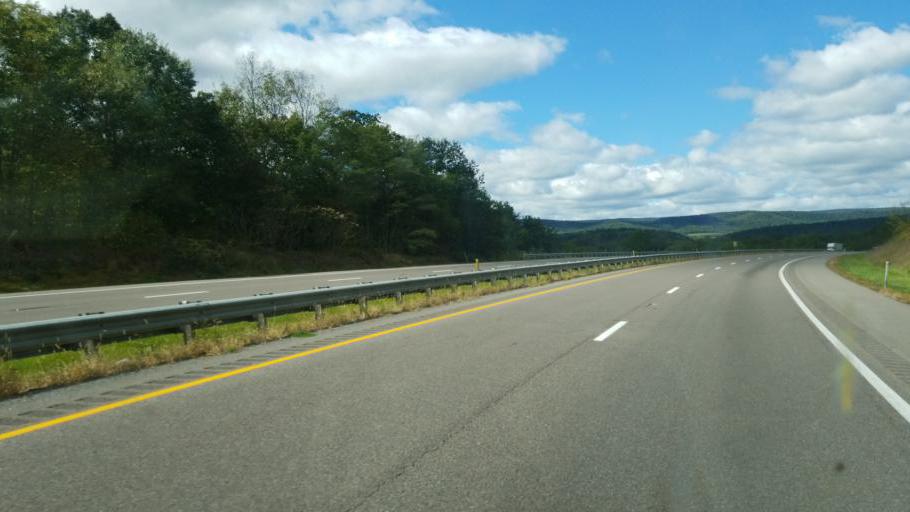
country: US
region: Maryland
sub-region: Allegany County
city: Cumberland
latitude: 39.6991
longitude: -78.5600
